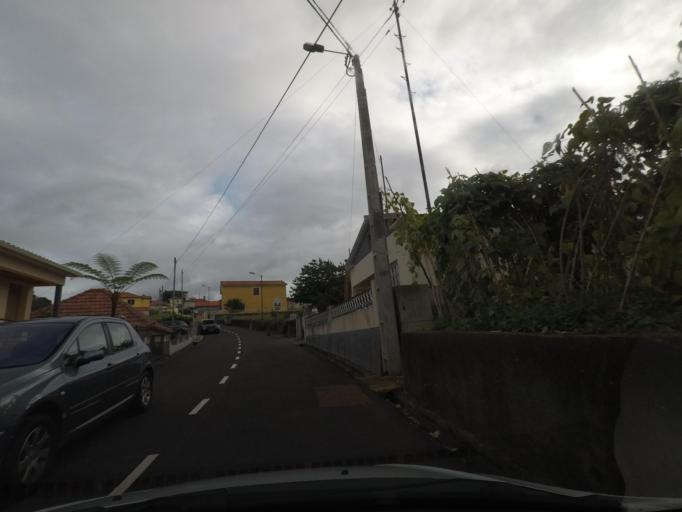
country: PT
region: Madeira
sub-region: Santana
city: Santana
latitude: 32.8084
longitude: -16.8768
